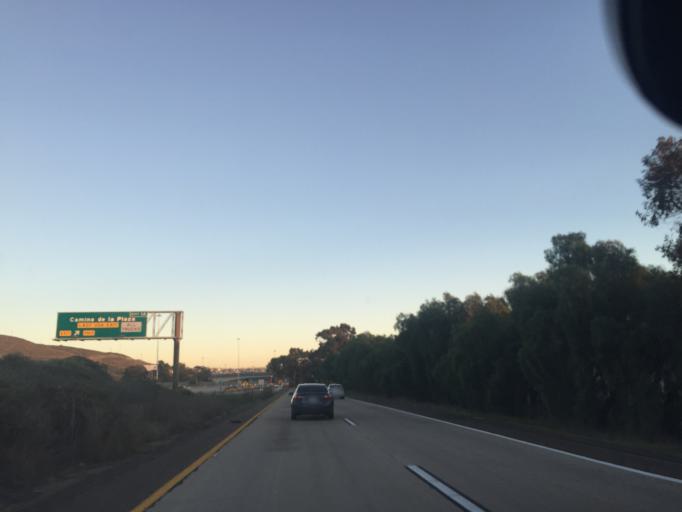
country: MX
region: Baja California
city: Tijuana
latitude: 32.5467
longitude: -117.0377
